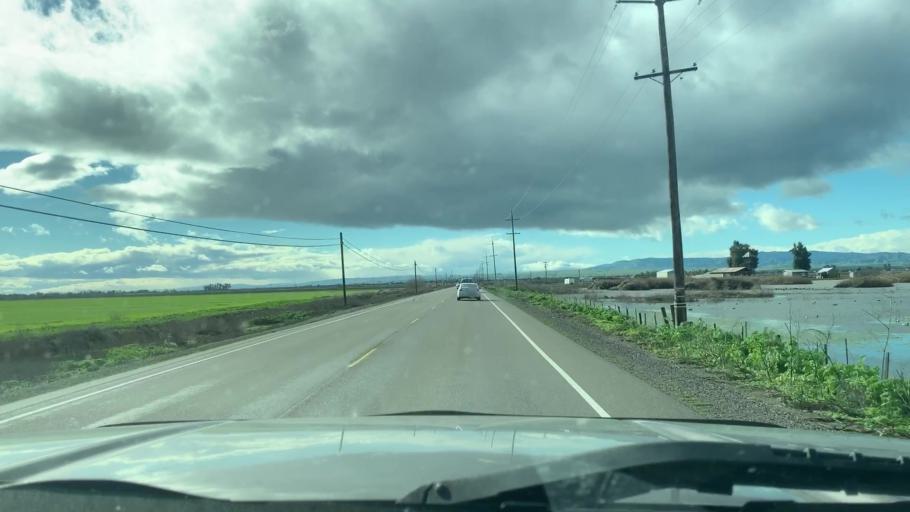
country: US
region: California
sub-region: Merced County
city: Los Banos
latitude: 37.1295
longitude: -120.8348
